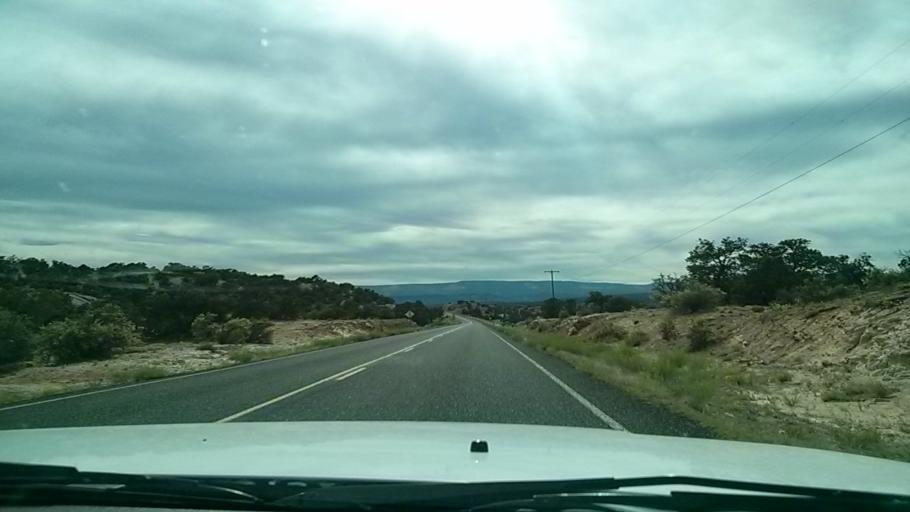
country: US
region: Utah
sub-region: Wayne County
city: Loa
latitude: 37.7506
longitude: -111.4595
